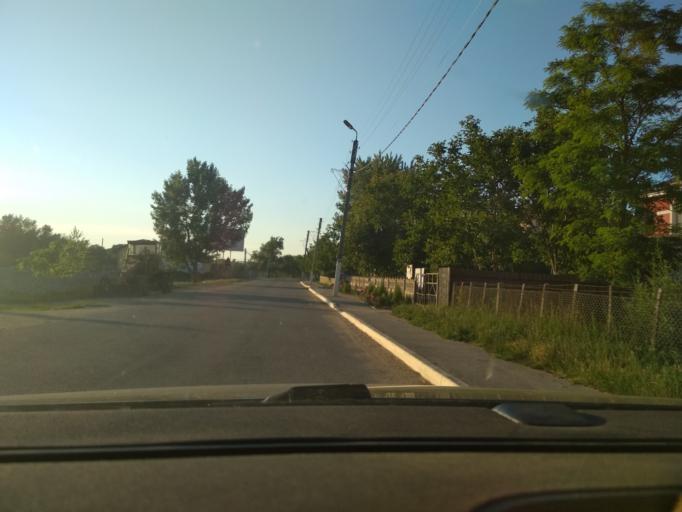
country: RO
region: Iasi
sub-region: Comuna Grozesti
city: Grozesti
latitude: 47.0016
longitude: 28.0779
